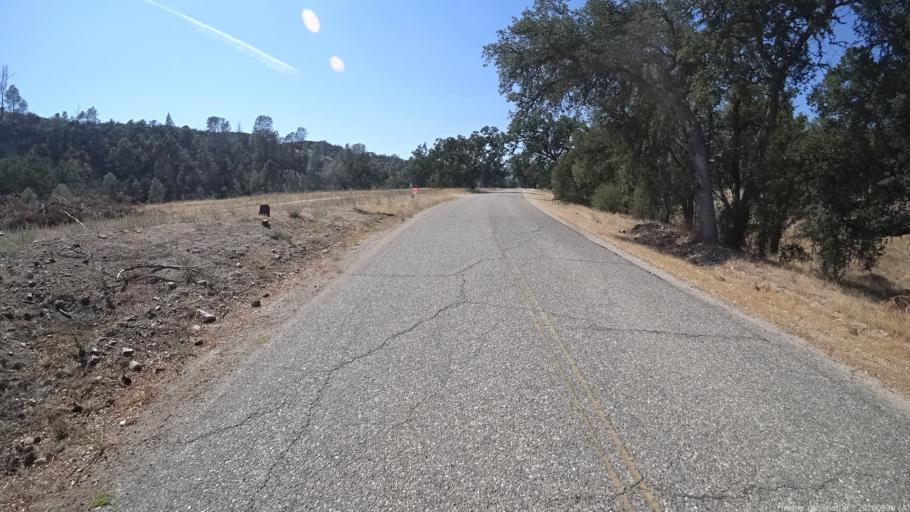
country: US
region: California
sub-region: Monterey County
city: King City
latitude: 36.0024
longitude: -121.2641
